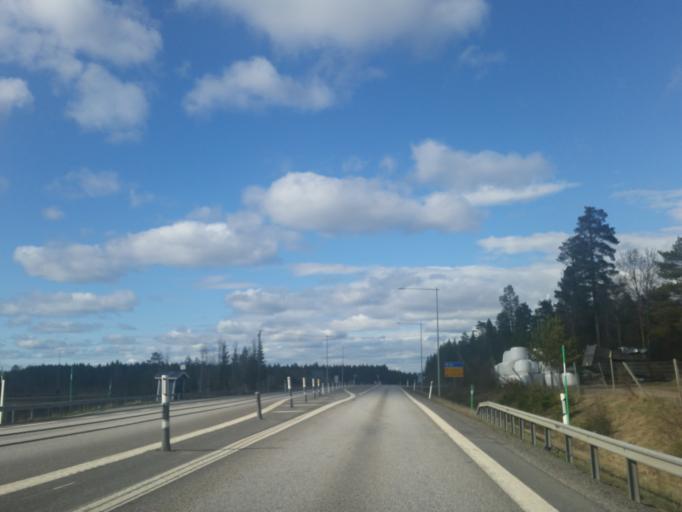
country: SE
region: Vaesterbotten
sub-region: Robertsfors Kommun
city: Robertsfors
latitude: 64.1164
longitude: 20.8812
